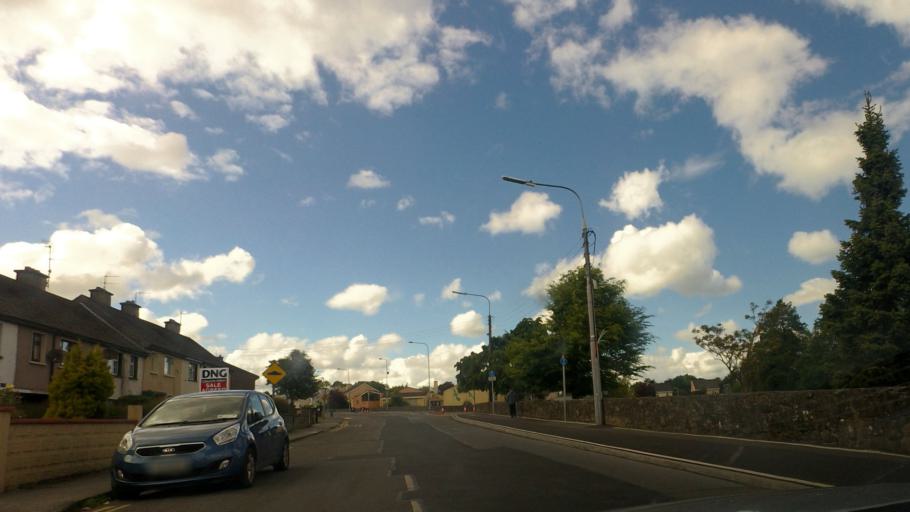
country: IE
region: Munster
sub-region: An Clar
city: Ennis
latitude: 52.8466
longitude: -8.9918
